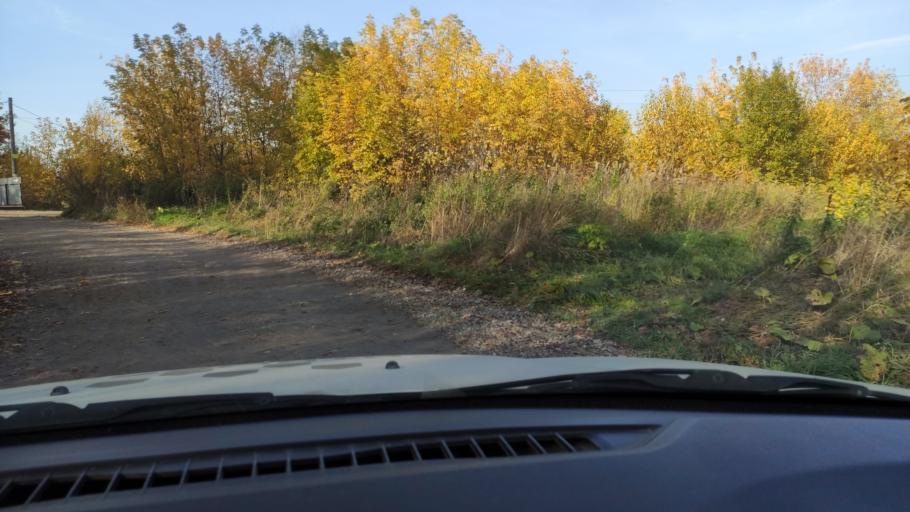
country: RU
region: Perm
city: Sylva
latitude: 58.0452
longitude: 56.7391
